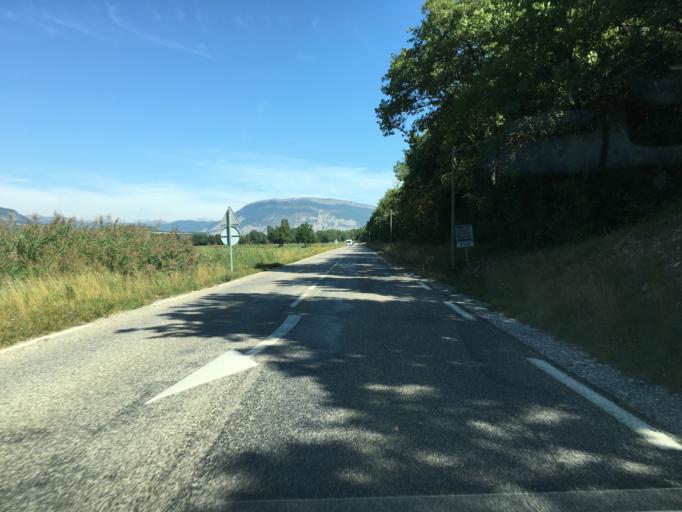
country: FR
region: Provence-Alpes-Cote d'Azur
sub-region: Departement des Hautes-Alpes
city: Serres
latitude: 44.4533
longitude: 5.7255
